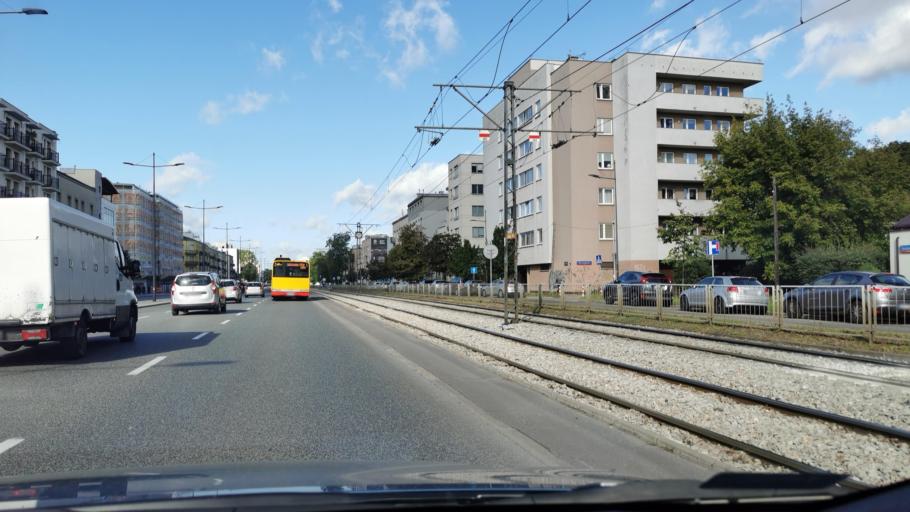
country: PL
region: Masovian Voivodeship
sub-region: Warszawa
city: Praga Poludnie
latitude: 52.2405
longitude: 21.1113
